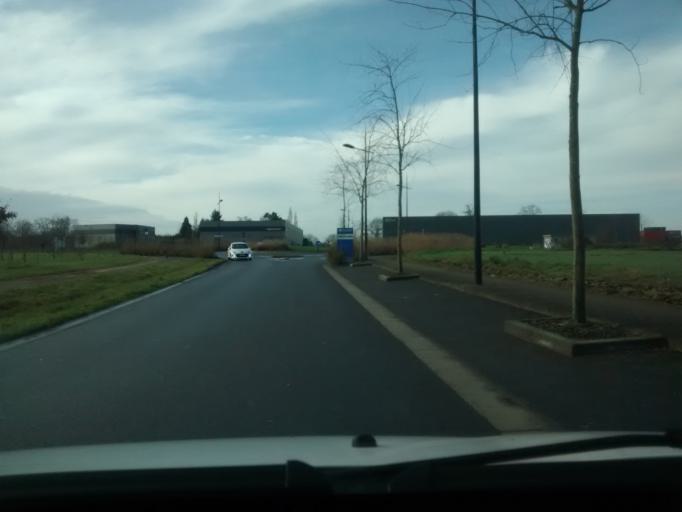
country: FR
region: Brittany
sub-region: Departement d'Ille-et-Vilaine
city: Pace
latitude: 48.1459
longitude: -1.7565
